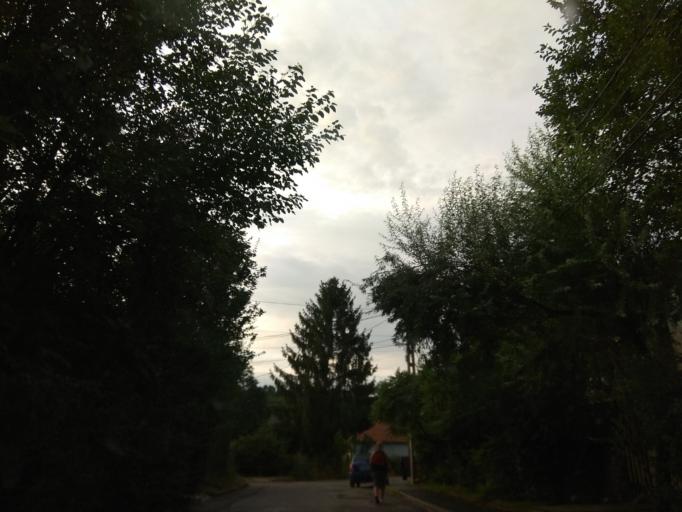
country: HU
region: Borsod-Abauj-Zemplen
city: Miskolc
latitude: 48.0548
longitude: 20.7818
